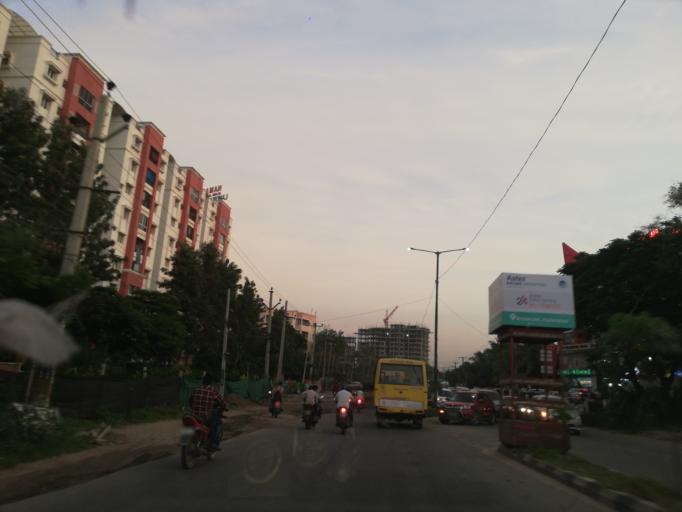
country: IN
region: Telangana
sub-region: Rangareddi
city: Kukatpalli
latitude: 17.5072
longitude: 78.3623
